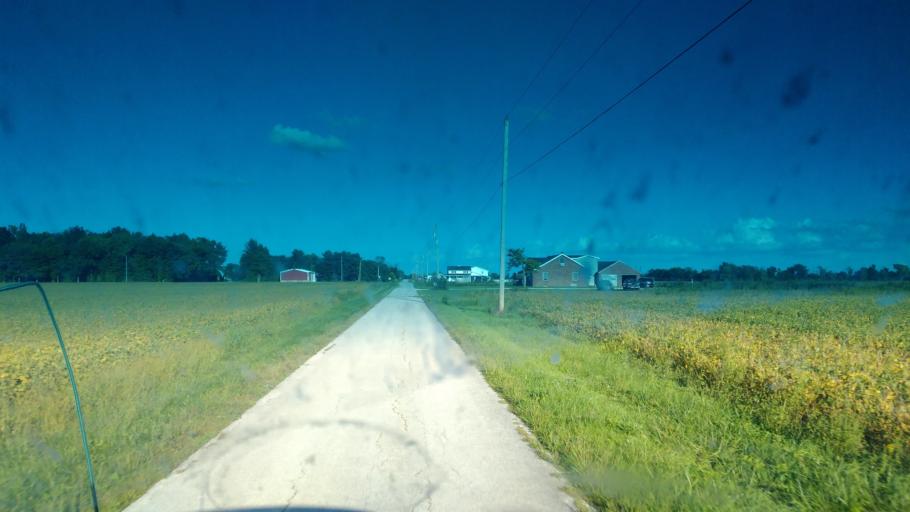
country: US
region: Ohio
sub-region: Wyandot County
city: Carey
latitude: 40.9412
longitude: -83.4510
